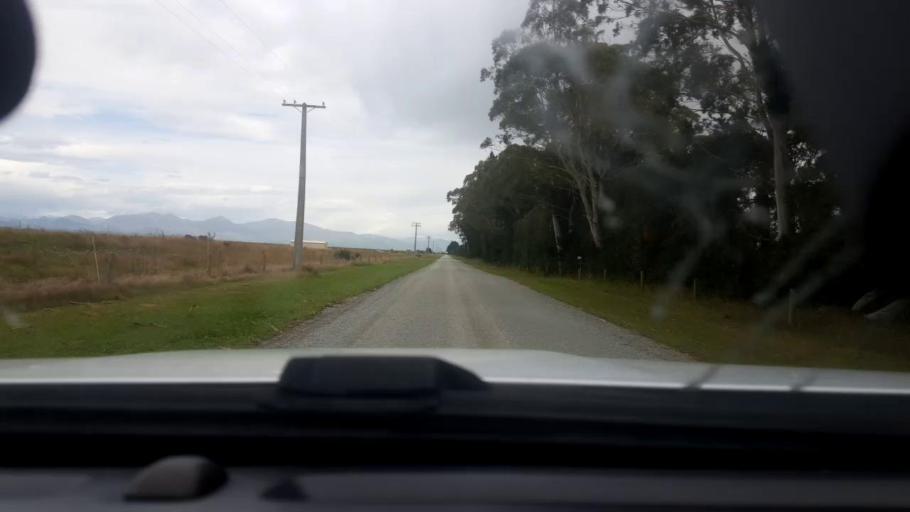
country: NZ
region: Canterbury
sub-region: Timaru District
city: Pleasant Point
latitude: -44.1510
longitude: 171.3945
